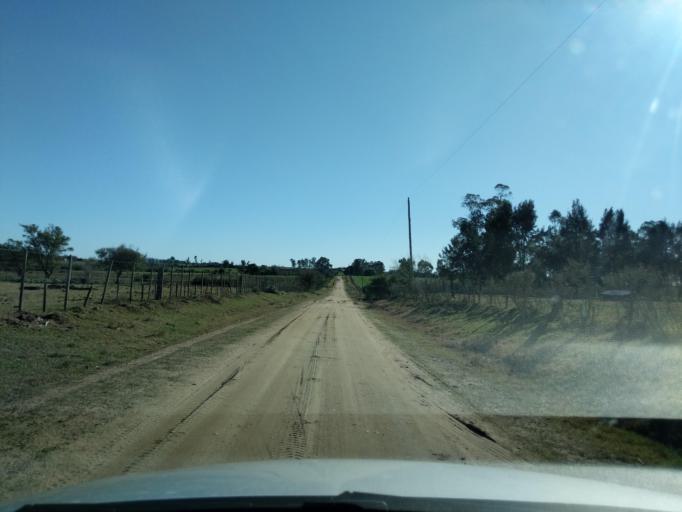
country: UY
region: Florida
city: Florida
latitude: -34.0745
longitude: -56.2678
